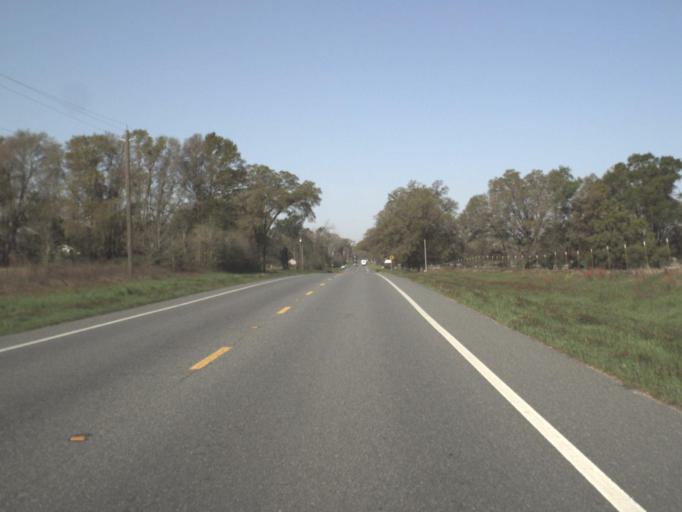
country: US
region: Florida
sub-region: Jackson County
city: Malone
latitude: 30.9571
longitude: -85.1431
